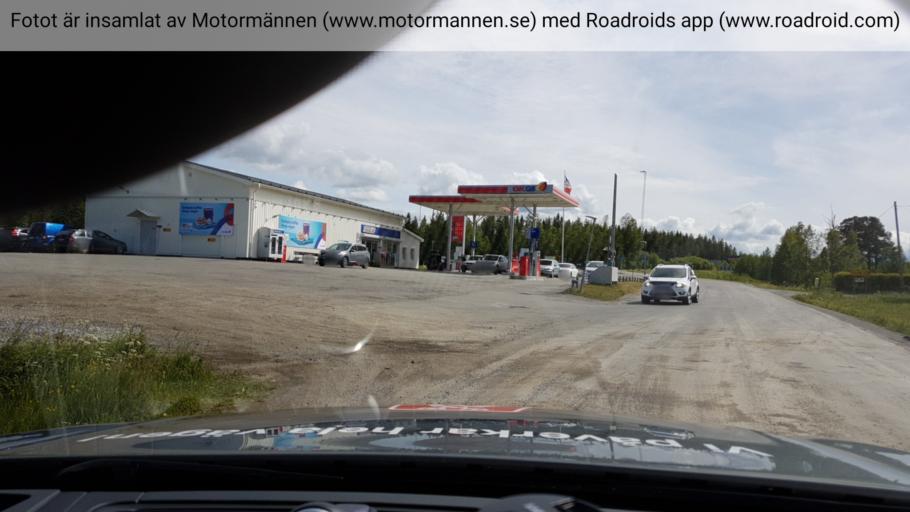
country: SE
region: Jaemtland
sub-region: Bergs Kommun
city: Hoverberg
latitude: 62.7533
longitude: 14.4273
